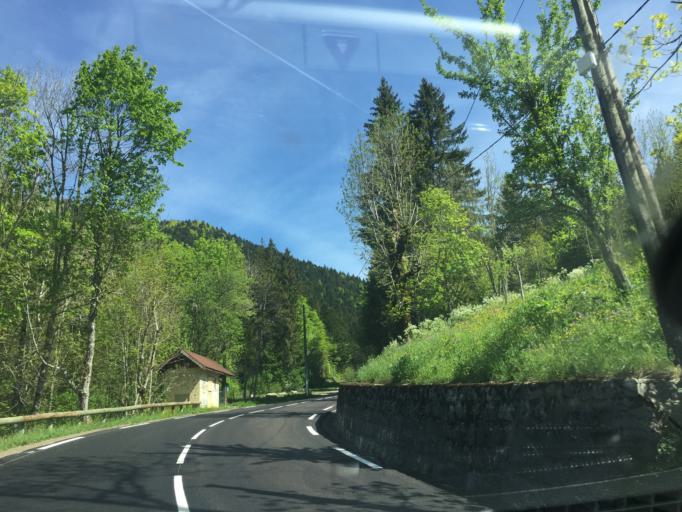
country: FR
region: Rhone-Alpes
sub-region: Departement de l'Isere
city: Saint-Hilaire
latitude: 45.3596
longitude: 5.8297
